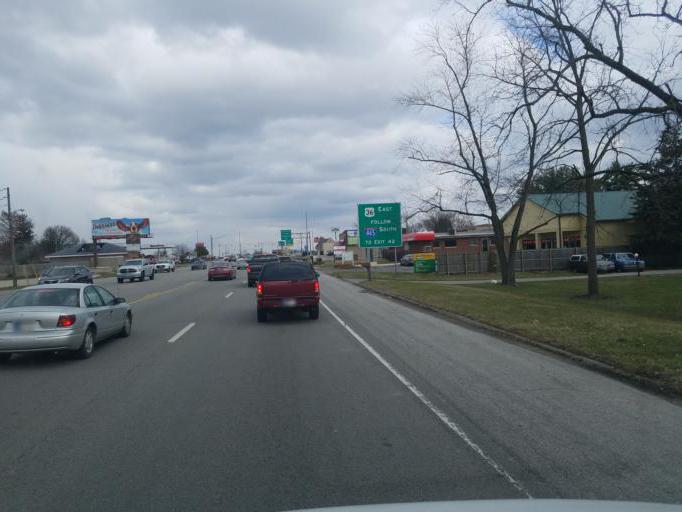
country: US
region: Indiana
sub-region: Marion County
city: Speedway
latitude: 39.7646
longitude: -86.2728
